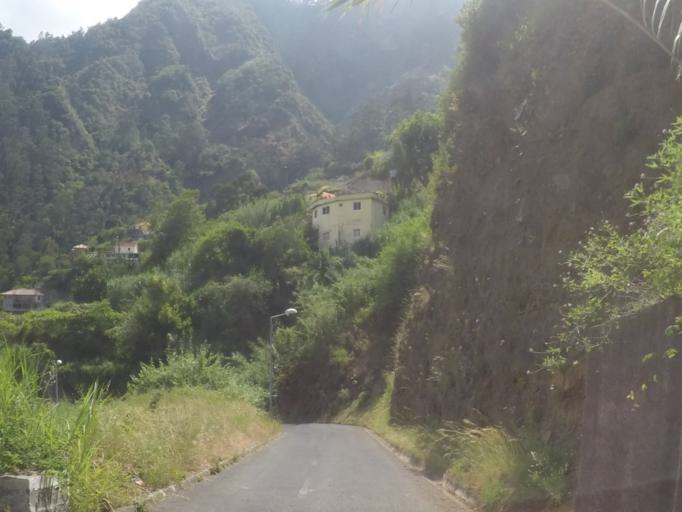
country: PT
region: Madeira
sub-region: Camara de Lobos
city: Curral das Freiras
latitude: 32.7077
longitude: -16.9724
